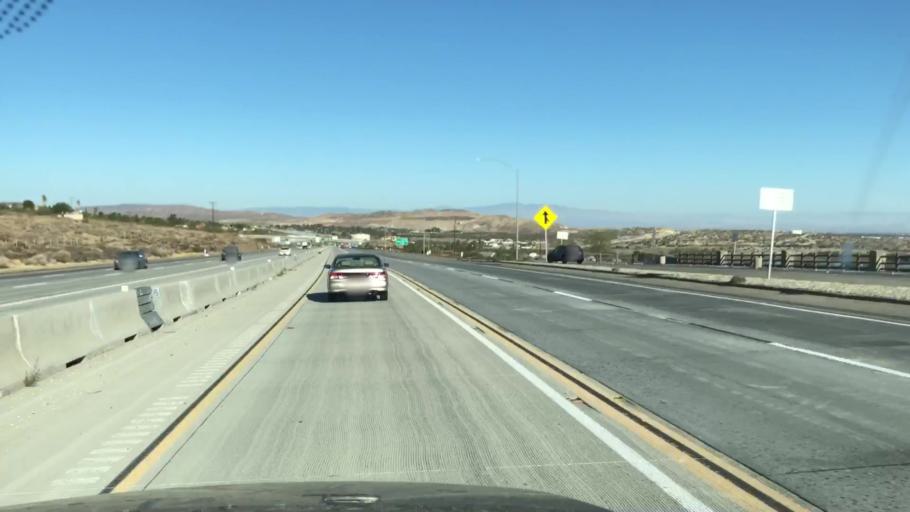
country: US
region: California
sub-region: Los Angeles County
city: Palmdale
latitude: 34.5418
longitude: -118.1222
